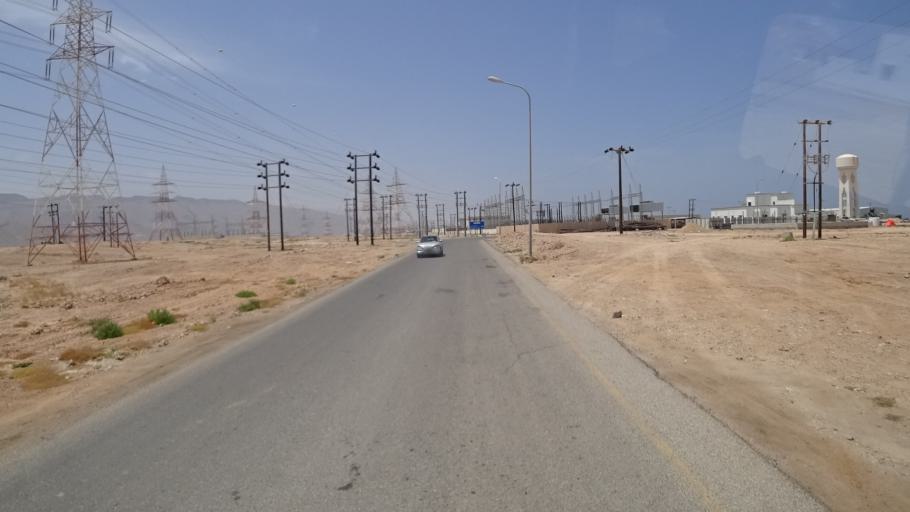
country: OM
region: Ash Sharqiyah
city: Sur
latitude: 22.6167
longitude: 59.4545
